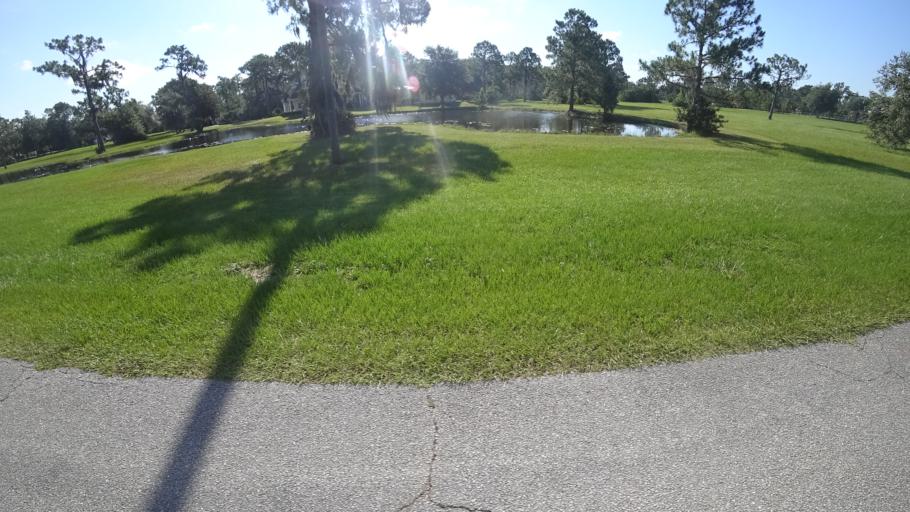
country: US
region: Florida
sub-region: Sarasota County
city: The Meadows
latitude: 27.4162
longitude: -82.3472
